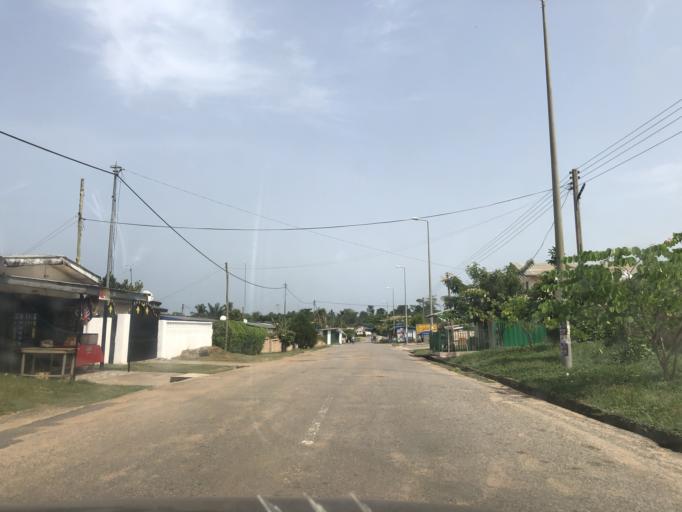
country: GH
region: Eastern
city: Koforidua
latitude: 6.0911
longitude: -0.2731
